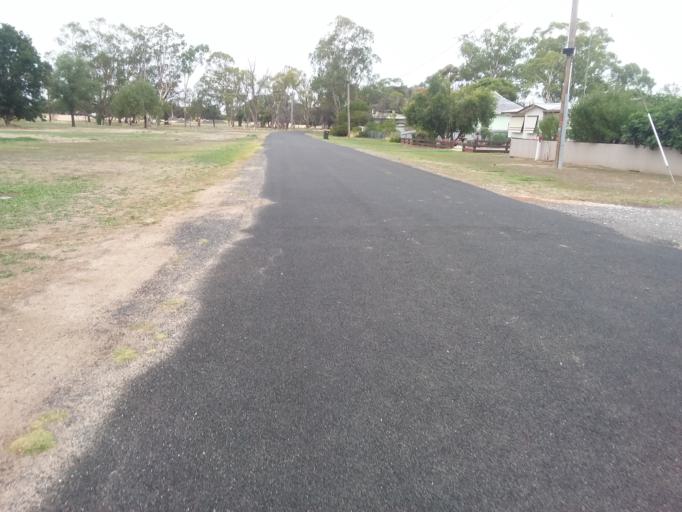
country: AU
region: Victoria
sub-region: Horsham
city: Horsham
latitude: -36.7407
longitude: 141.9382
